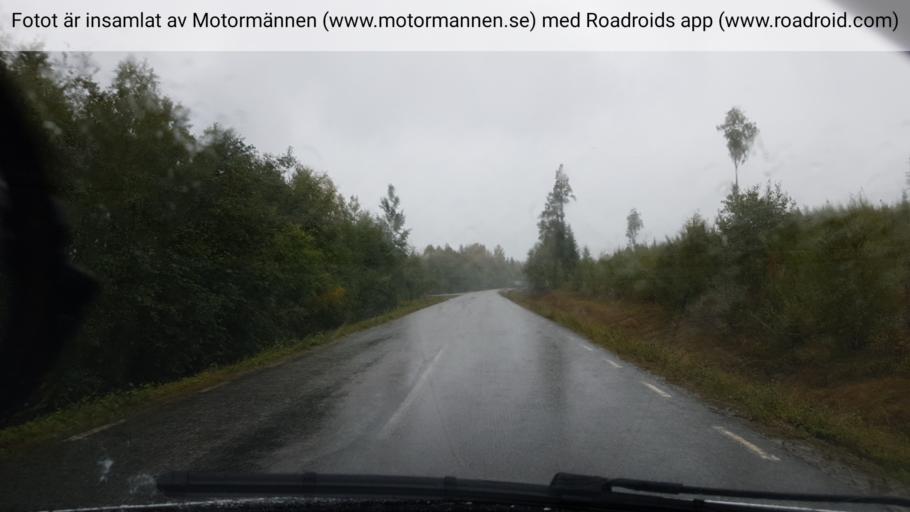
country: SE
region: Vaesterbotten
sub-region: Vannas Kommun
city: Vannasby
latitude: 64.0477
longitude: 19.9344
